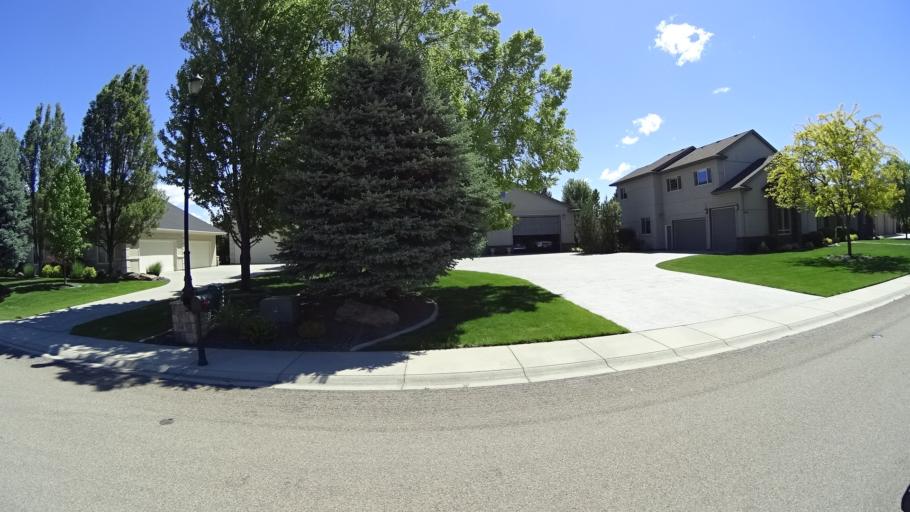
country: US
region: Idaho
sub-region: Ada County
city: Eagle
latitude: 43.6667
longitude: -116.3804
